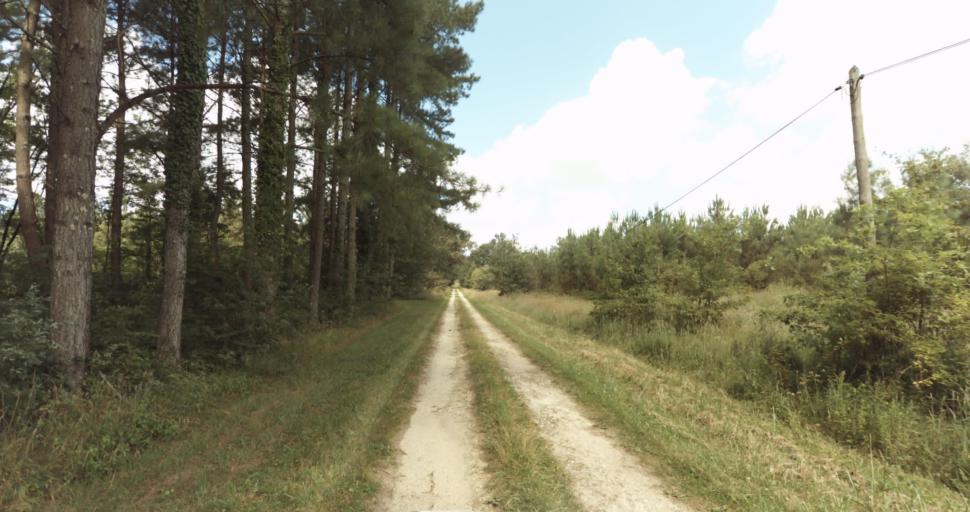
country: FR
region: Aquitaine
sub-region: Departement de la Gironde
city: Bazas
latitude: 44.4572
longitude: -0.1866
